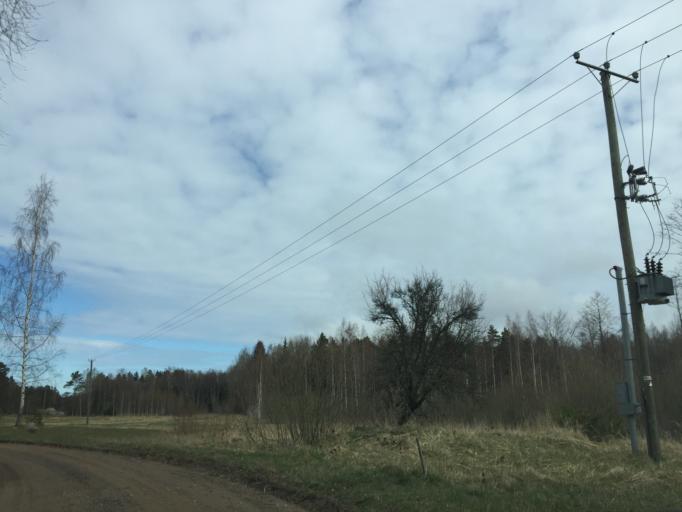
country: LV
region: Salacgrivas
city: Salacgriva
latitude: 57.5271
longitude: 24.3787
